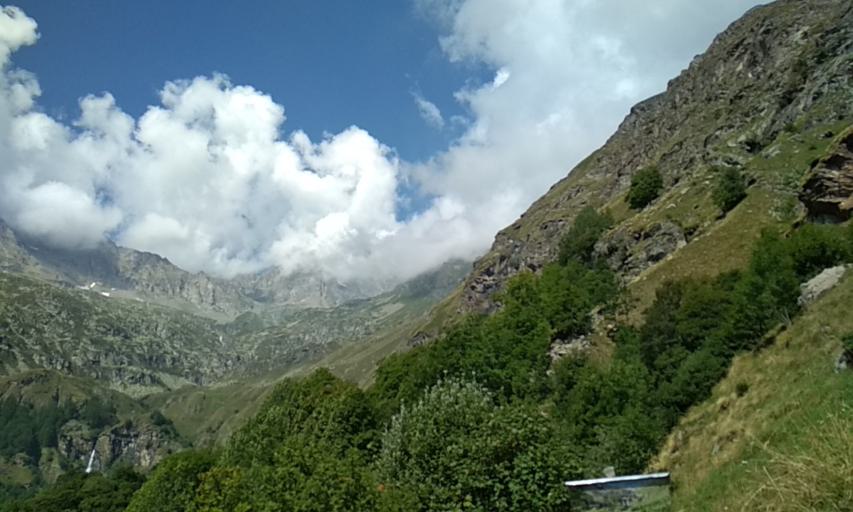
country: IT
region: Piedmont
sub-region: Provincia di Torino
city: Noasca
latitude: 45.4581
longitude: 7.2874
